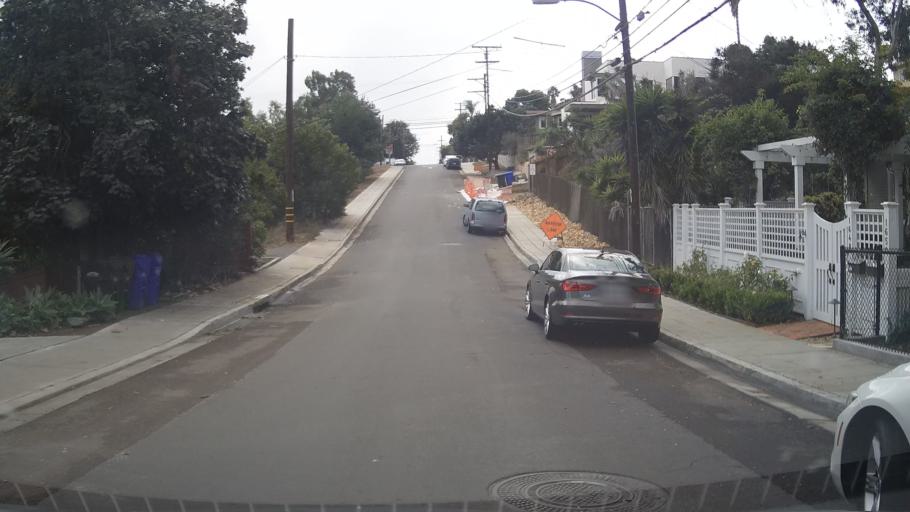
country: US
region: California
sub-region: San Diego County
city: San Diego
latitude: 32.7234
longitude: -117.1276
